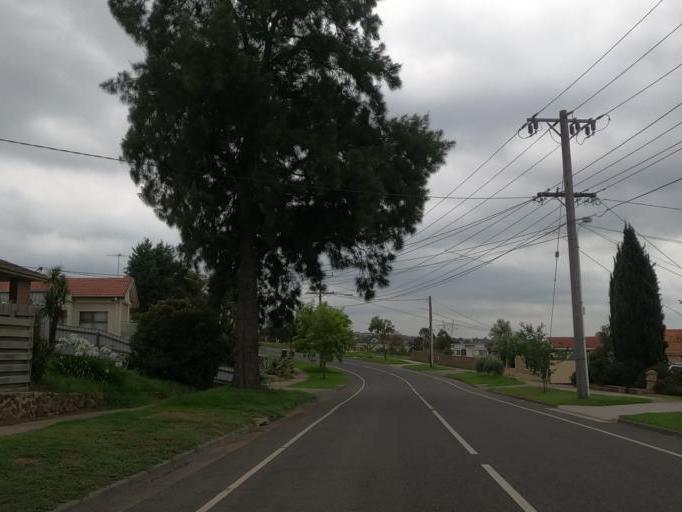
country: AU
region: Victoria
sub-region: Hume
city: Broadmeadows
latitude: -37.6694
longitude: 144.9092
